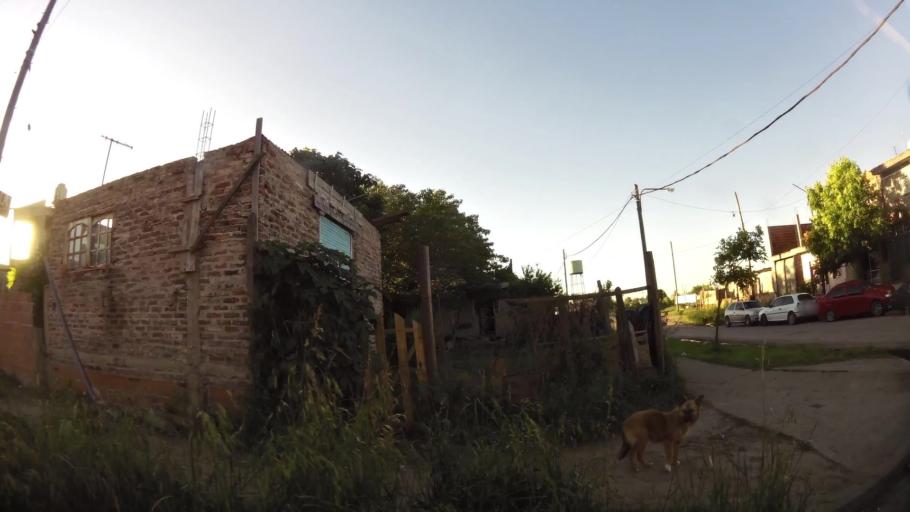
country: AR
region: Buenos Aires
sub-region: Partido de Almirante Brown
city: Adrogue
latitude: -34.7708
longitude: -58.3283
